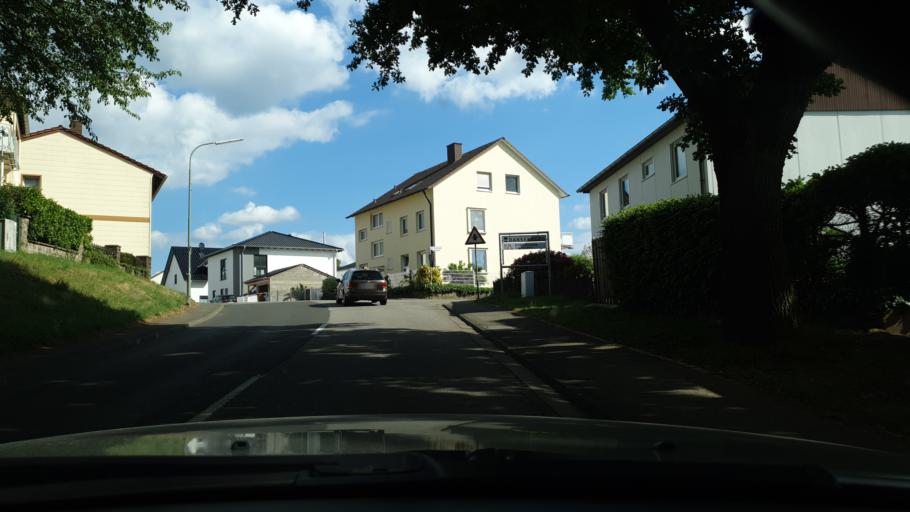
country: DE
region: Rheinland-Pfalz
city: Stelzenberg
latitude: 49.4073
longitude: 7.7224
